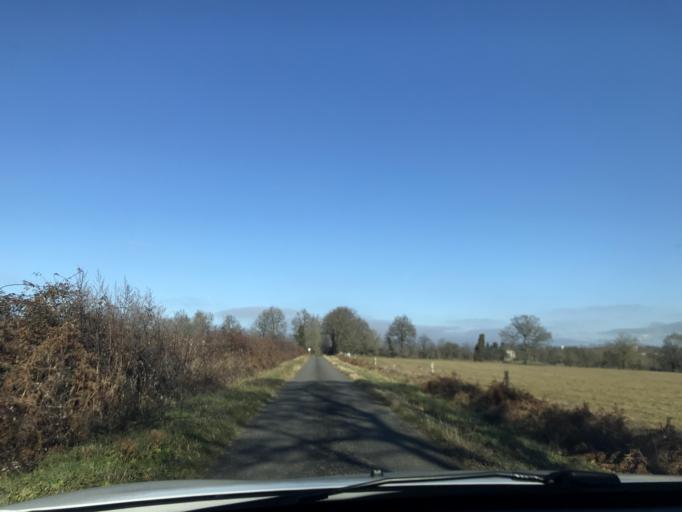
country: FR
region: Poitou-Charentes
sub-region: Departement de la Charente
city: Saint-Claud
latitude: 45.8584
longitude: 0.5317
